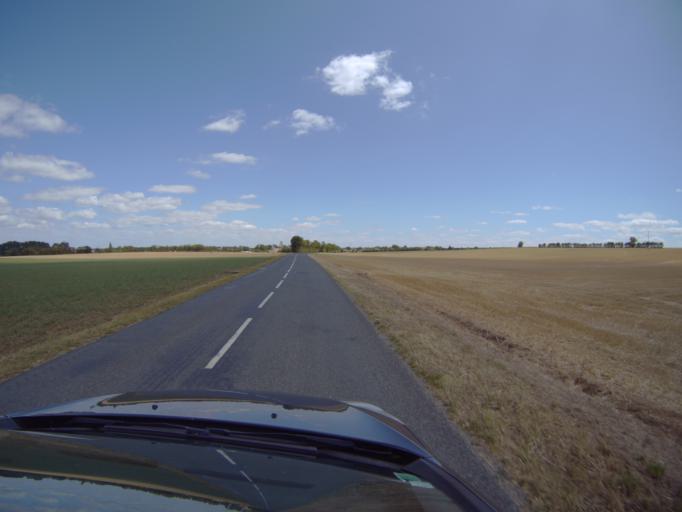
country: FR
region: Poitou-Charentes
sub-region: Departement de la Charente-Maritime
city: Courcon
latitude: 46.2488
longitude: -0.8248
